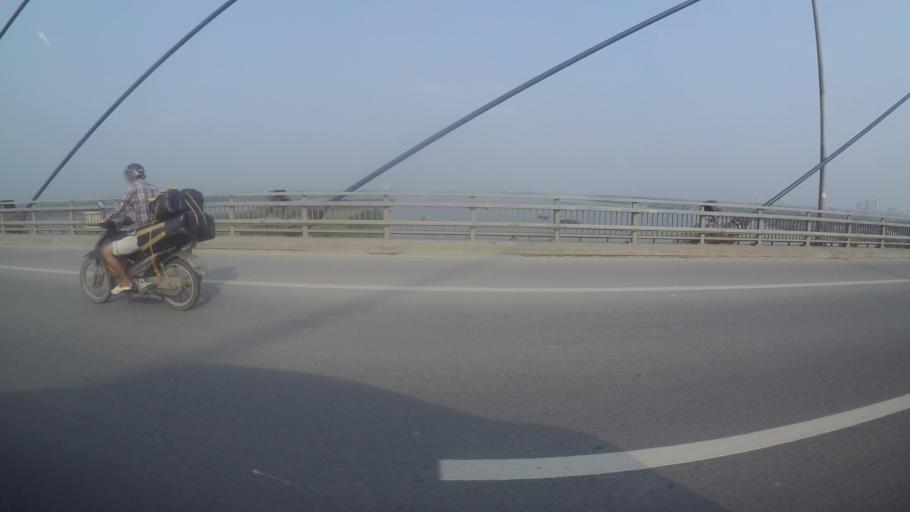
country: VN
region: Ha Noi
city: Tay Ho
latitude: 21.0923
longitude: 105.8204
